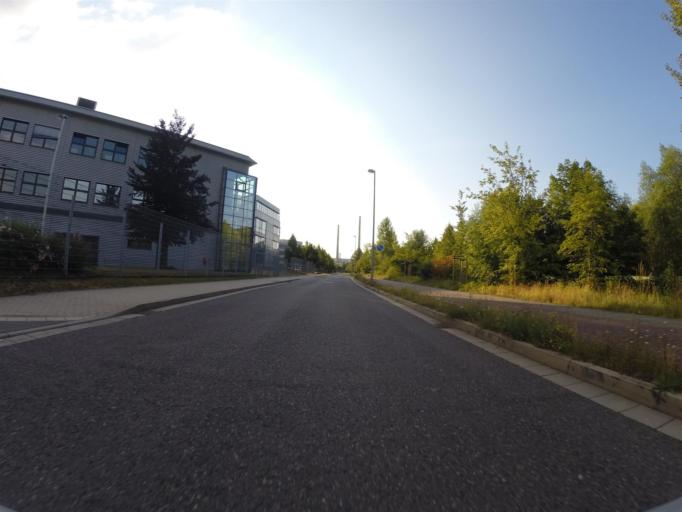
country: DE
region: Thuringia
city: Sulza
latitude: 50.8893
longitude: 11.5981
